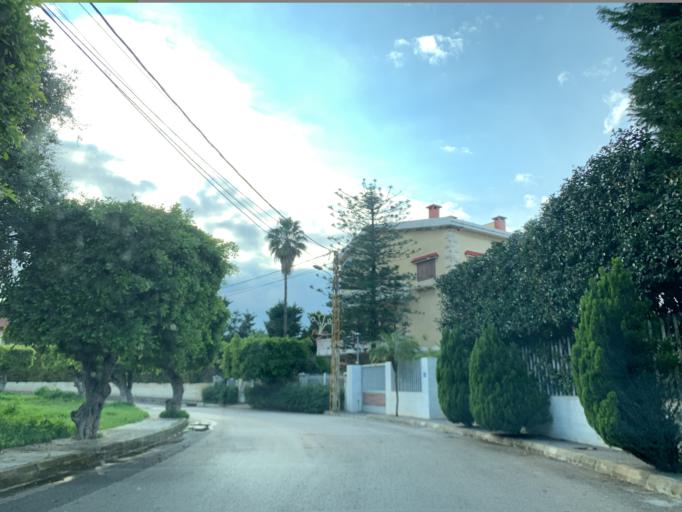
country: LB
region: Mont-Liban
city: Baabda
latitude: 33.8522
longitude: 35.5755
